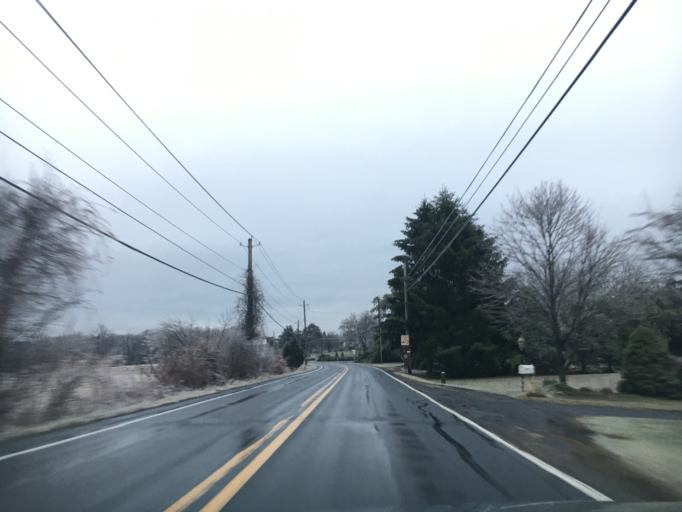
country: US
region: Pennsylvania
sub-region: Lehigh County
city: Schnecksville
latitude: 40.6250
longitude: -75.6216
